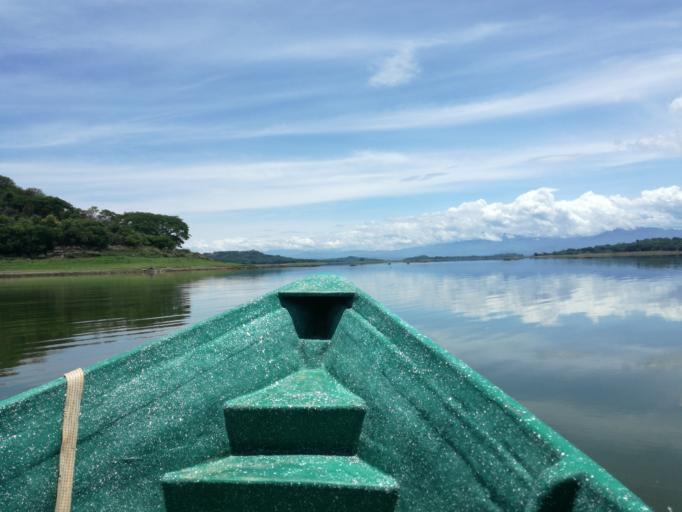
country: SV
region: Cuscatlan
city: Suchitoto
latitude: 13.9442
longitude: -89.0065
